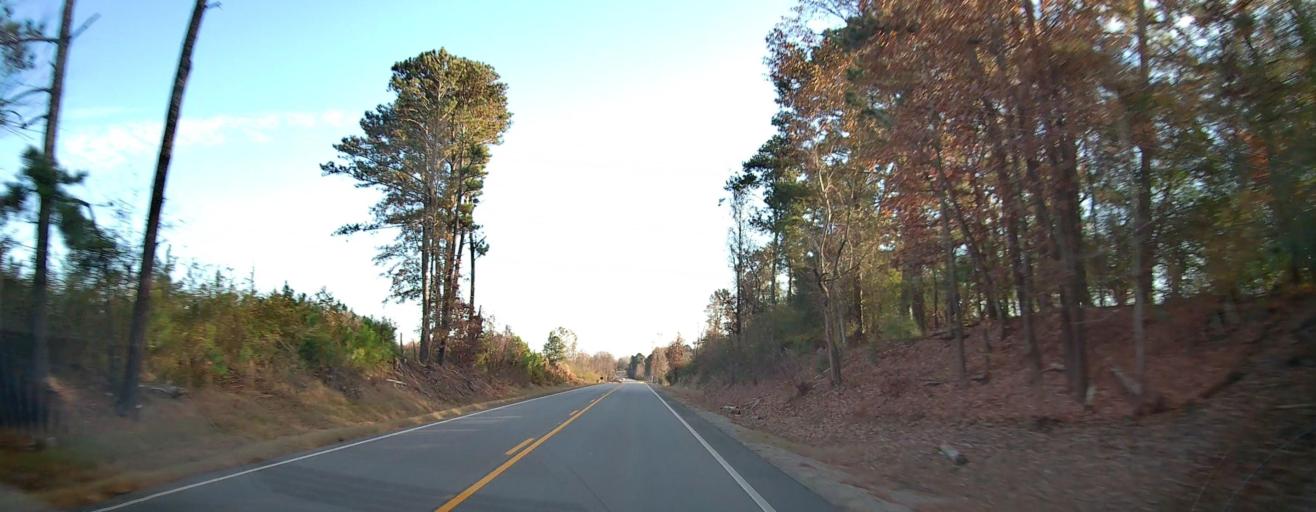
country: US
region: Alabama
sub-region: Marshall County
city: Arab
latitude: 34.2559
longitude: -86.5708
